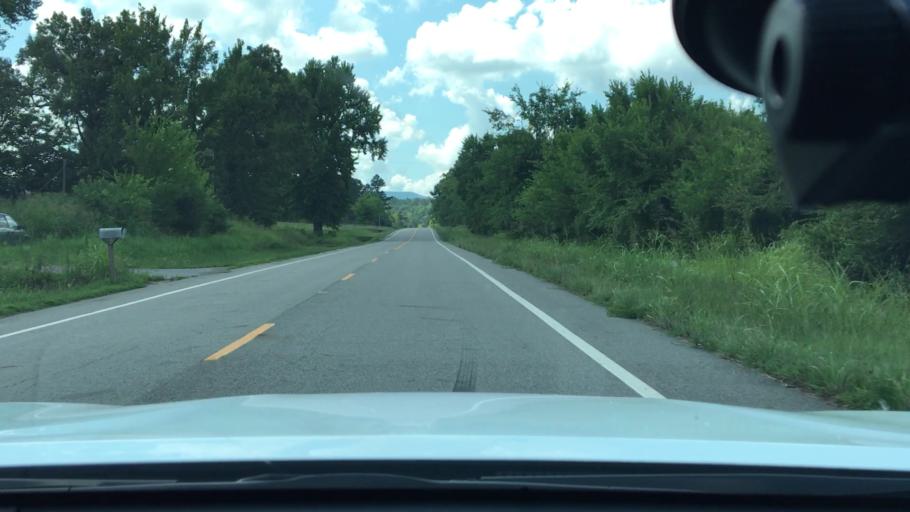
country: US
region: Arkansas
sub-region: Logan County
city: Paris
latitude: 35.2666
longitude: -93.6832
